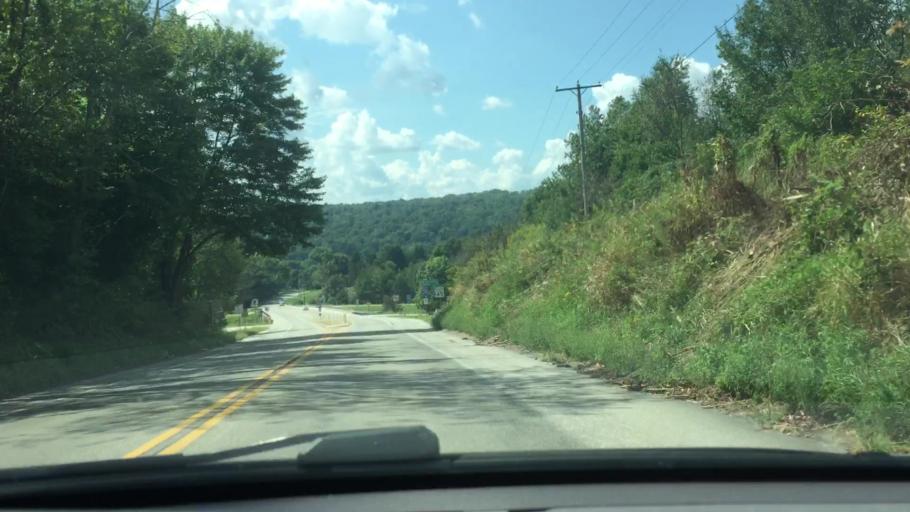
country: US
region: Pennsylvania
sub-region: Lawrence County
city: New Wilmington
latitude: 41.1144
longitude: -80.4232
